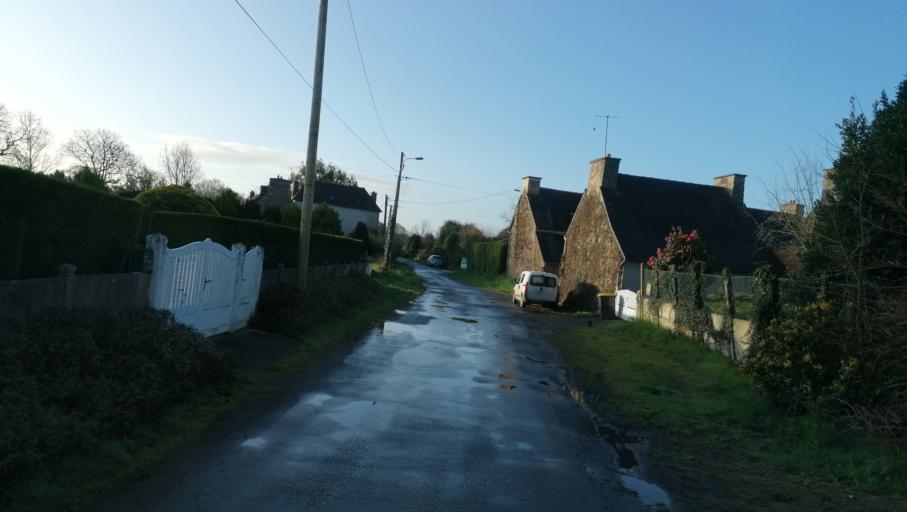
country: FR
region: Brittany
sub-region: Departement des Cotes-d'Armor
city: Plouha
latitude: 48.6668
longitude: -2.9151
